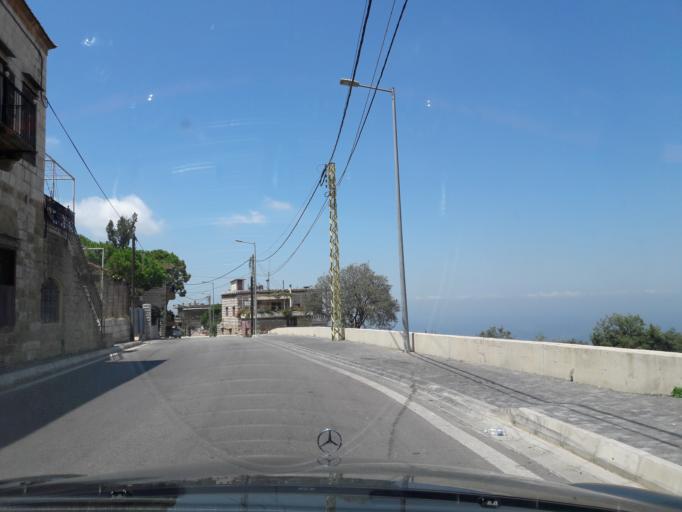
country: LB
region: Mont-Liban
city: Djounie
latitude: 33.9208
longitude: 35.6373
